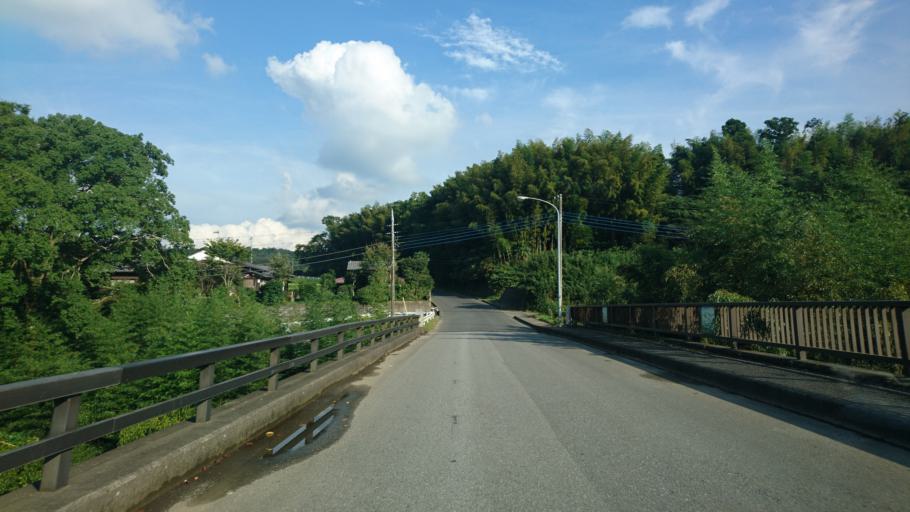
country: JP
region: Chiba
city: Kimitsu
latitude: 35.2797
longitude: 139.9870
